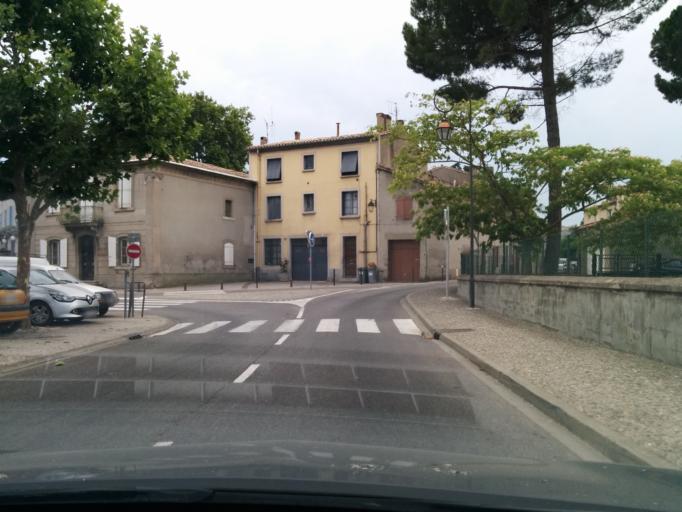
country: FR
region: Languedoc-Roussillon
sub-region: Departement de l'Aude
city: Carcassonne
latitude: 43.2096
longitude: 2.3604
